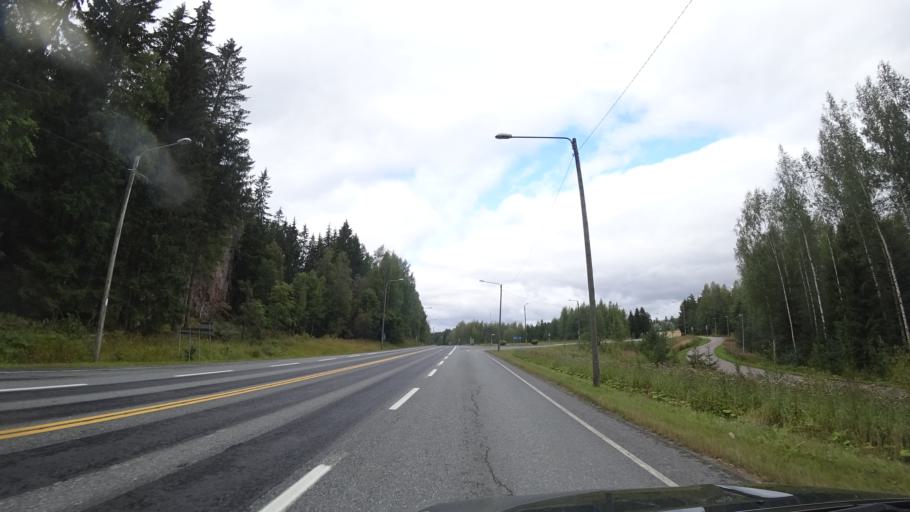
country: FI
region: Haeme
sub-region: Haemeenlinna
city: Lammi
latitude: 61.0530
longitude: 25.0068
